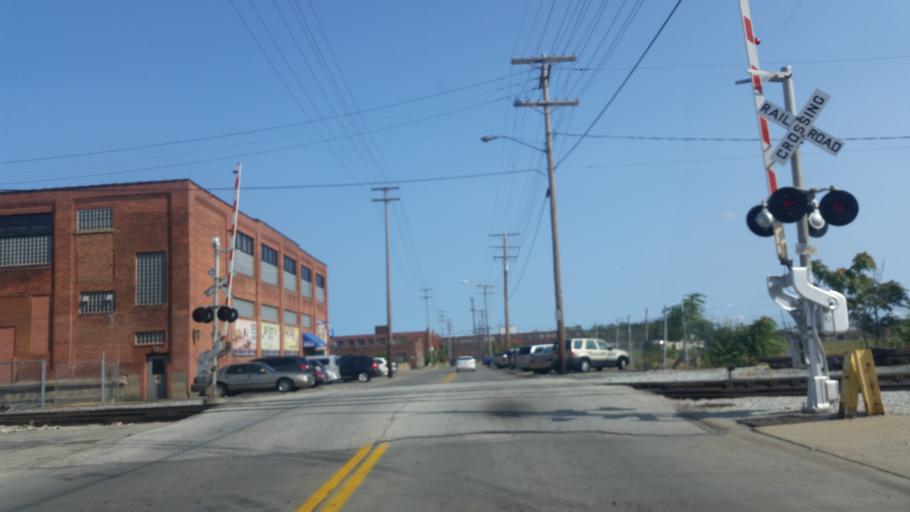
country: US
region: Ohio
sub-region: Cuyahoga County
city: Lakewood
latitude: 41.4734
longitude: -81.7627
